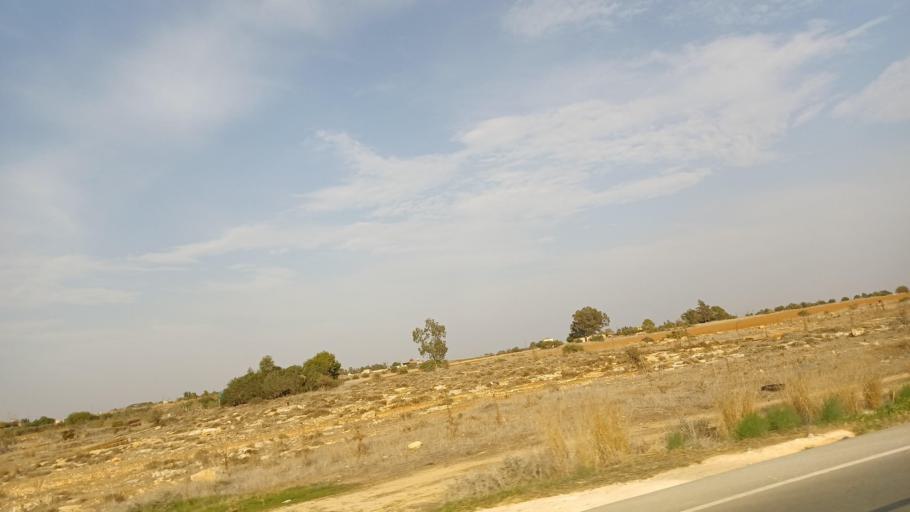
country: CY
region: Ammochostos
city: Frenaros
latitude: 35.0500
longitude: 33.9076
